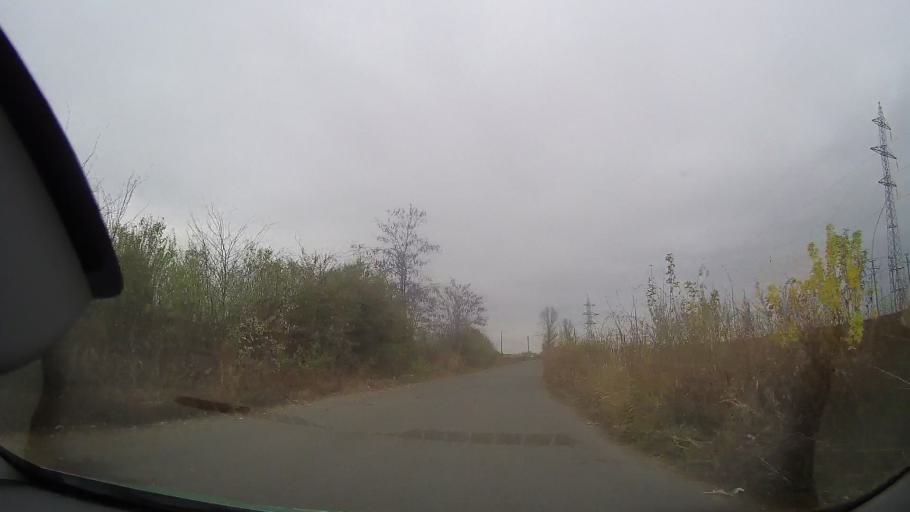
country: RO
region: Braila
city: Dudesti
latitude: 44.8963
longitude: 27.4333
